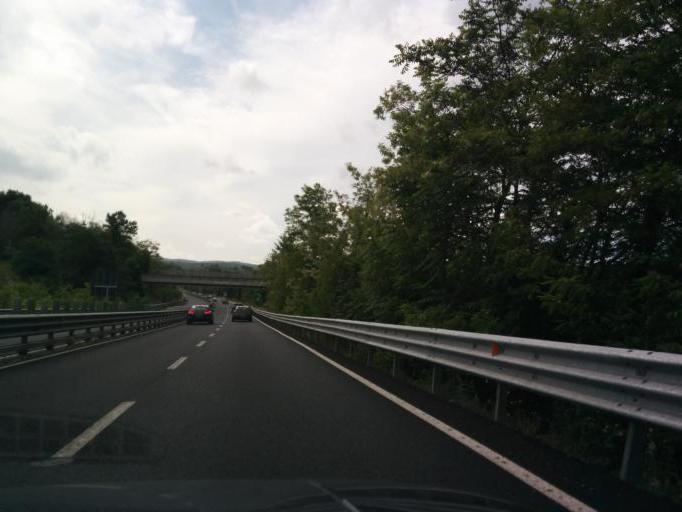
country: IT
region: Tuscany
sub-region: Province of Florence
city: Sambuca
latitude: 43.5465
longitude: 11.2117
